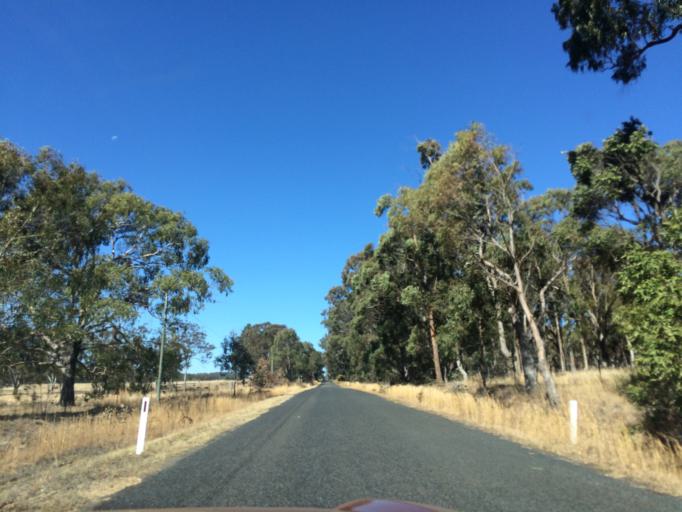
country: AU
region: Queensland
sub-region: Southern Downs
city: Stanthorpe
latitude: -28.6917
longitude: 152.0301
